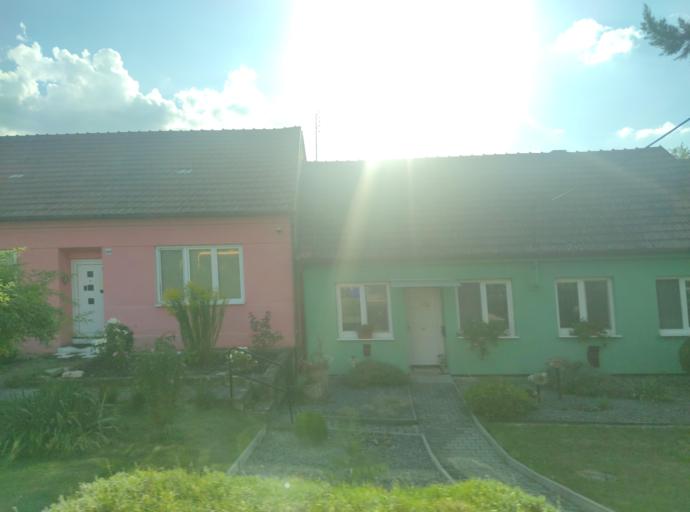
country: CZ
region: South Moravian
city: Vinicne Sumice
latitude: 49.1809
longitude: 16.8468
